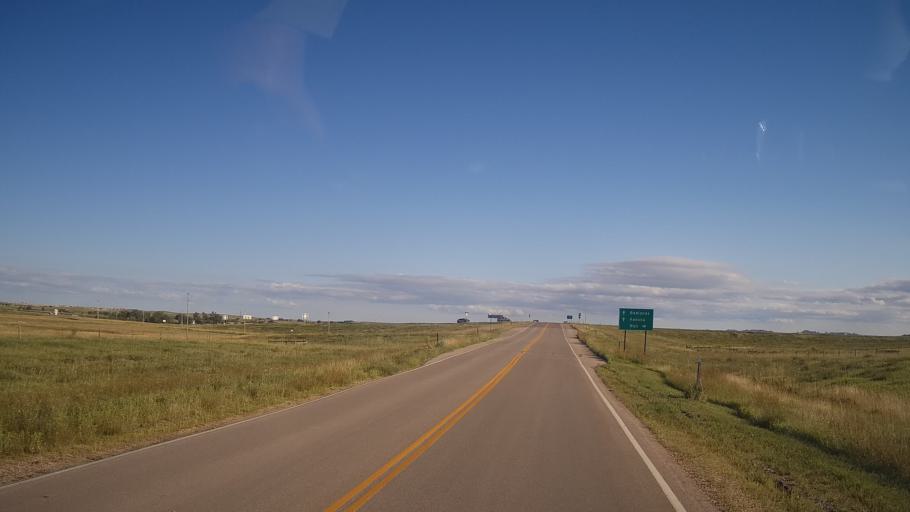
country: US
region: South Dakota
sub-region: Haakon County
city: Philip
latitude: 43.8443
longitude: -101.8997
